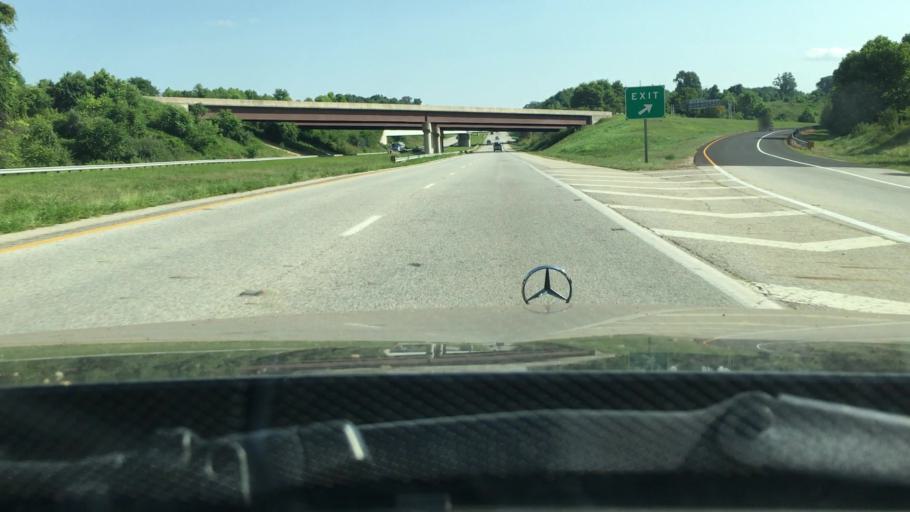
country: US
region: Virginia
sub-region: Amherst County
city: Amherst
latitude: 37.5568
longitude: -79.0666
